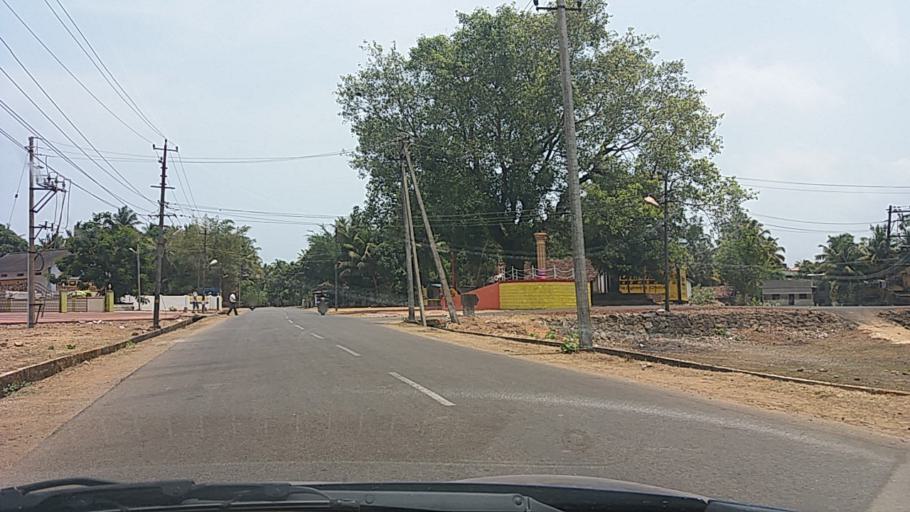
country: IN
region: Karnataka
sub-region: Uttar Kannada
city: Karwar
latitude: 14.8132
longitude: 74.1530
